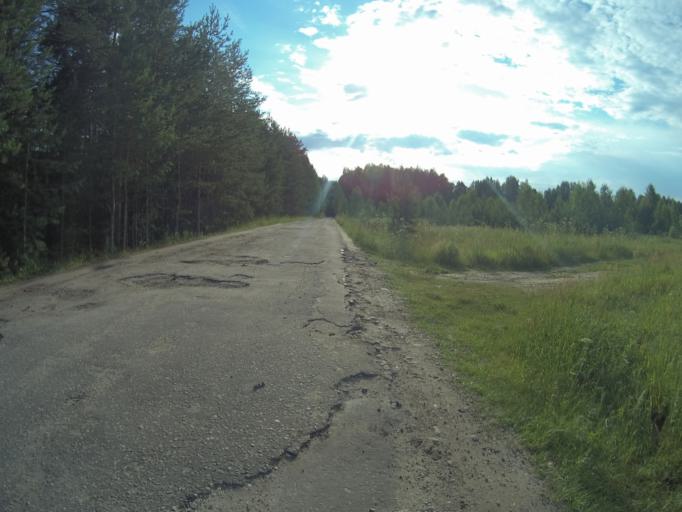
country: RU
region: Vladimir
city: Sudogda
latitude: 56.0318
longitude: 40.8641
